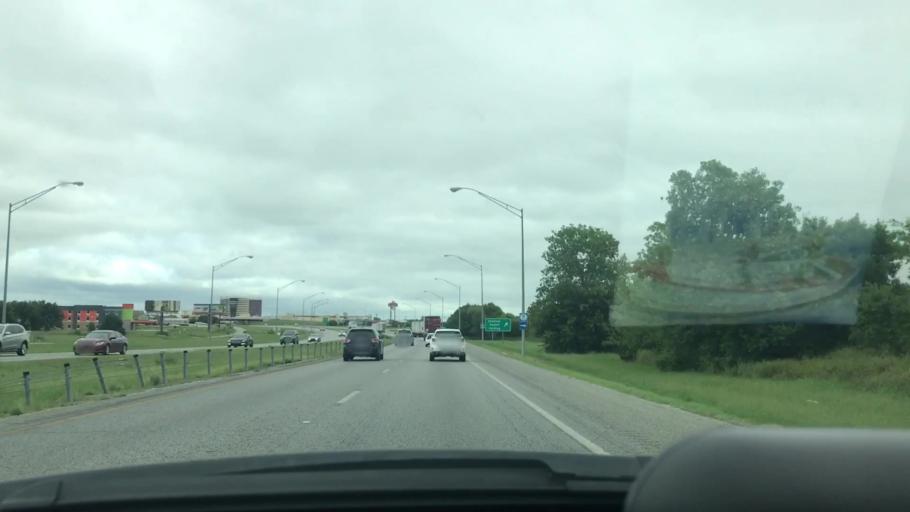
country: US
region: Oklahoma
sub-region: Bryan County
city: Calera
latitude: 33.9389
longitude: -96.4213
